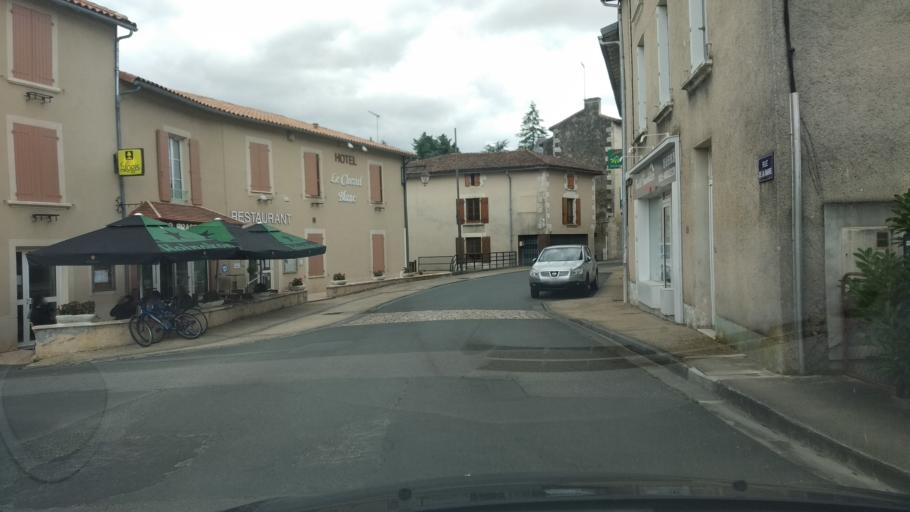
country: FR
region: Poitou-Charentes
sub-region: Departement de la Vienne
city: Vouille
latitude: 46.6393
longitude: 0.1654
